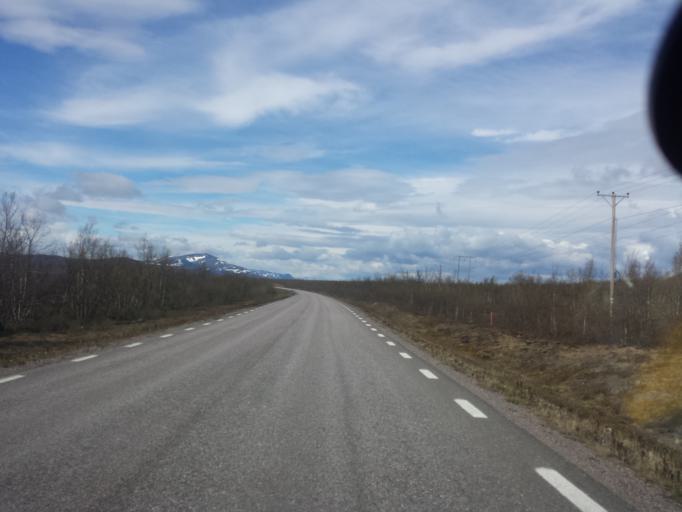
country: SE
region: Norrbotten
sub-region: Kiruna Kommun
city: Kiruna
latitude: 68.0491
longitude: 19.8304
